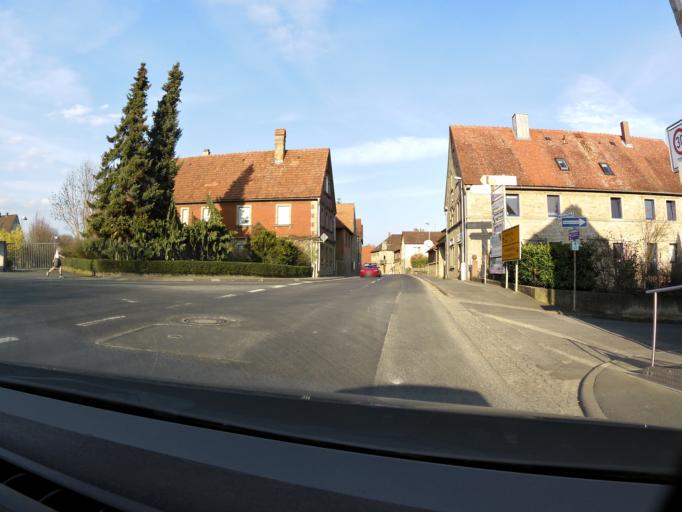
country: DE
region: Bavaria
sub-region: Regierungsbezirk Unterfranken
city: Kirchheim
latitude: 49.6562
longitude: 9.8573
